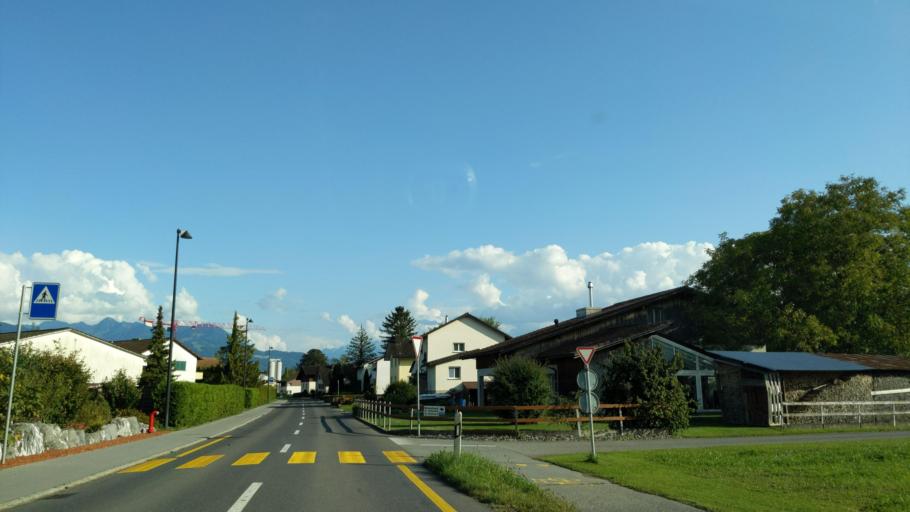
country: CH
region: Saint Gallen
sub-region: Wahlkreis Rheintal
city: Oberriet
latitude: 47.3278
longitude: 9.5637
